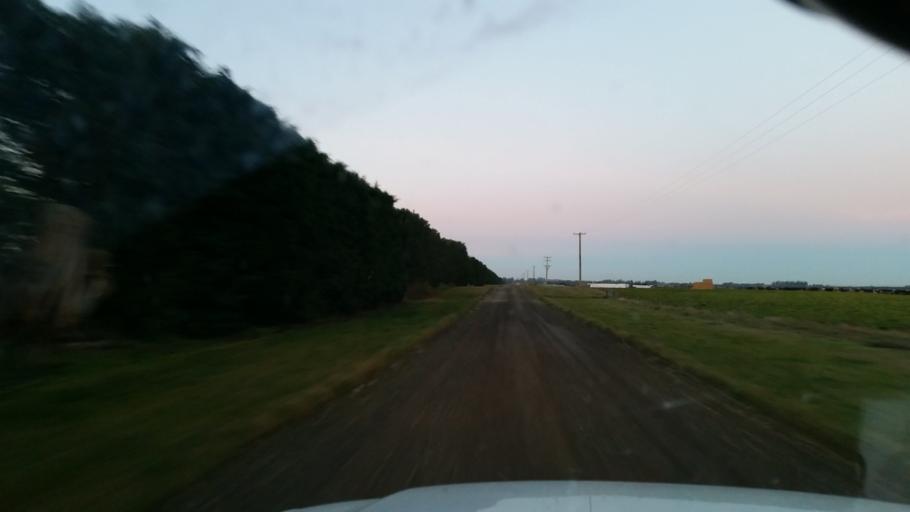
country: NZ
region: Canterbury
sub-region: Ashburton District
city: Tinwald
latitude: -43.9352
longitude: 171.5839
